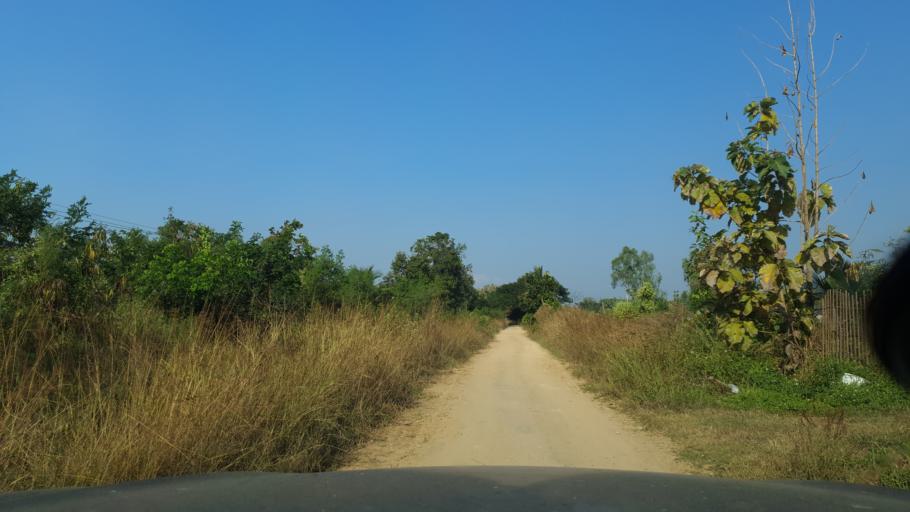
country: TH
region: Lamphun
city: Ban Thi
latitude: 18.6696
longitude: 99.1311
